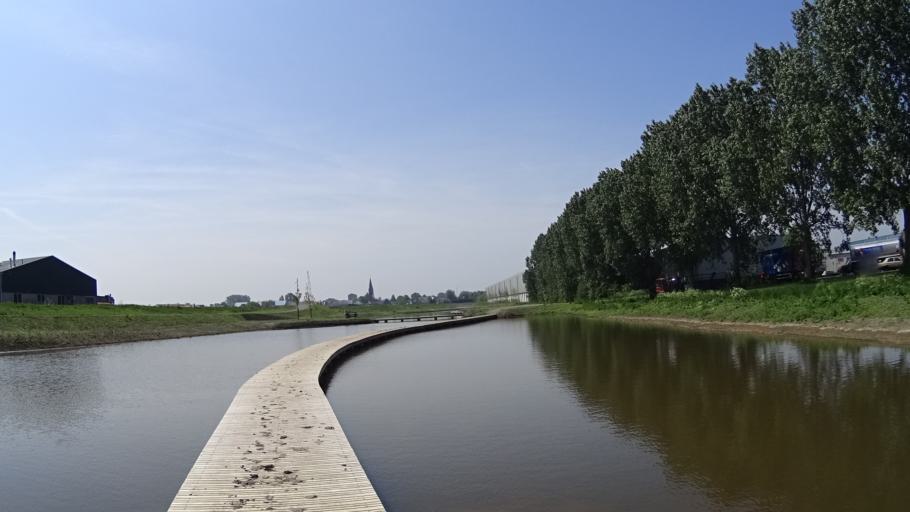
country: NL
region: South Holland
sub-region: Gemeente Pijnacker-Nootdorp
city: Pijnacker
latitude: 52.0259
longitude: 4.4457
